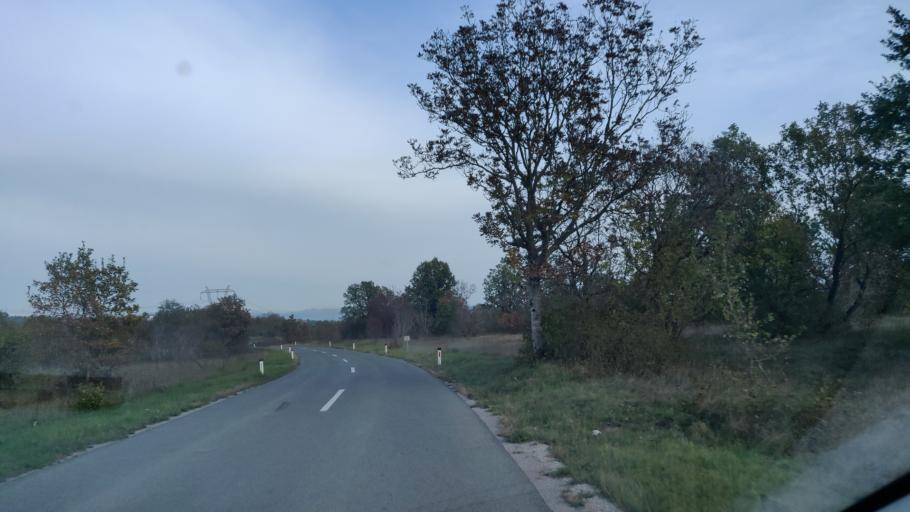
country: SI
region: Komen
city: Komen
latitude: 45.8143
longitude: 13.7885
